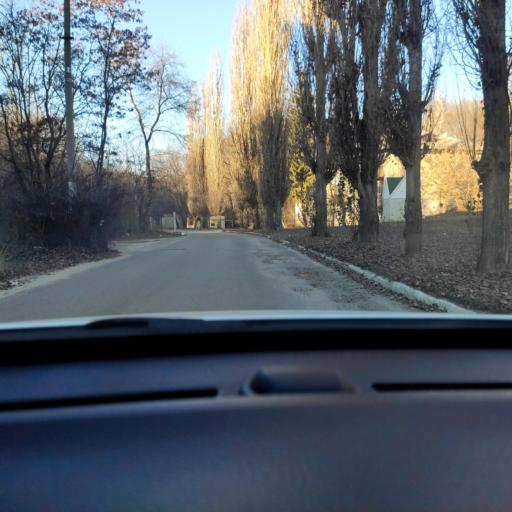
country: RU
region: Voronezj
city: Voronezh
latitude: 51.7259
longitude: 39.2336
